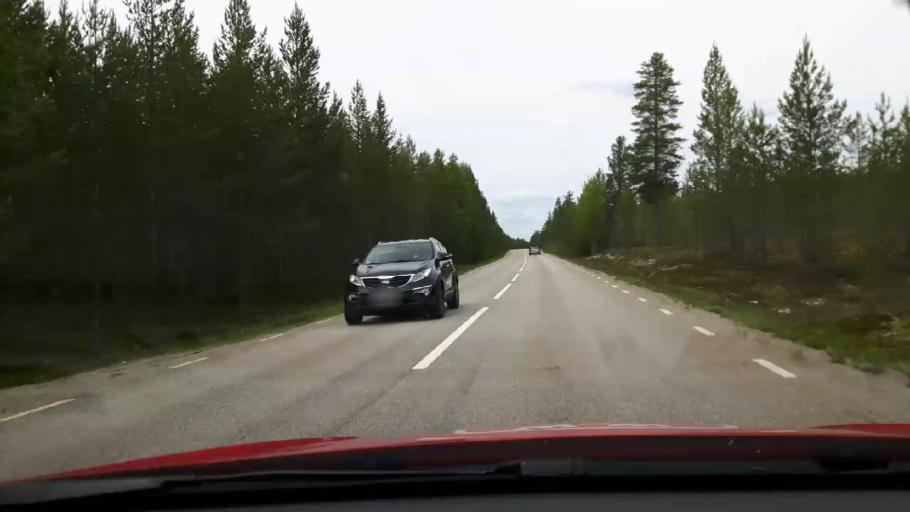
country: SE
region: Jaemtland
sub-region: Harjedalens Kommun
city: Sveg
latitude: 62.2372
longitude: 13.8518
